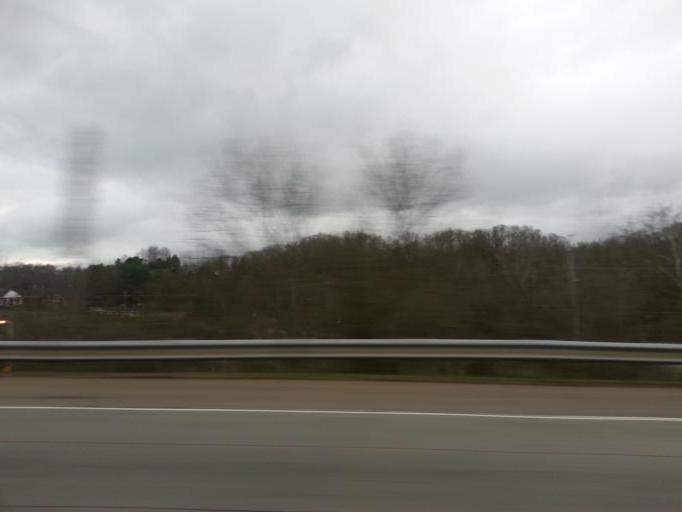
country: US
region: Tennessee
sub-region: Carter County
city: Central
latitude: 36.3285
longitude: -82.2699
